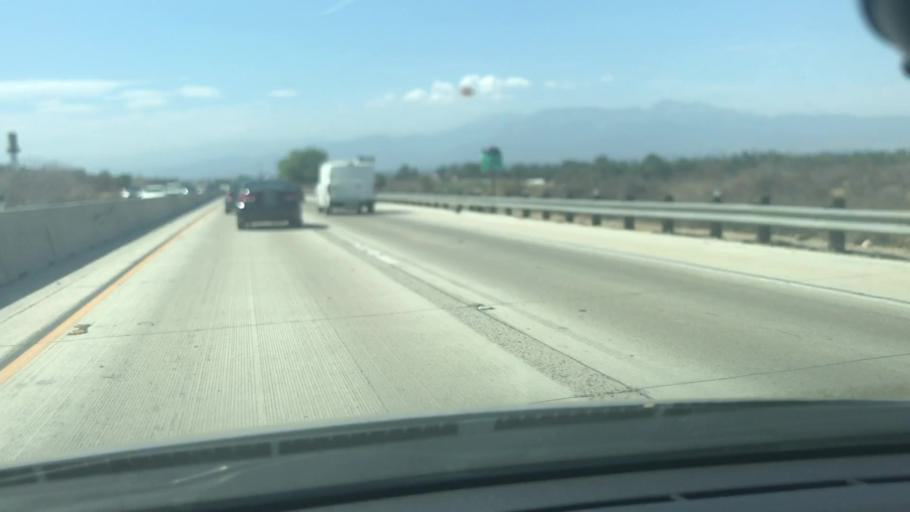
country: US
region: California
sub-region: San Bernardino County
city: Los Serranos
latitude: 33.9182
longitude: -117.6526
